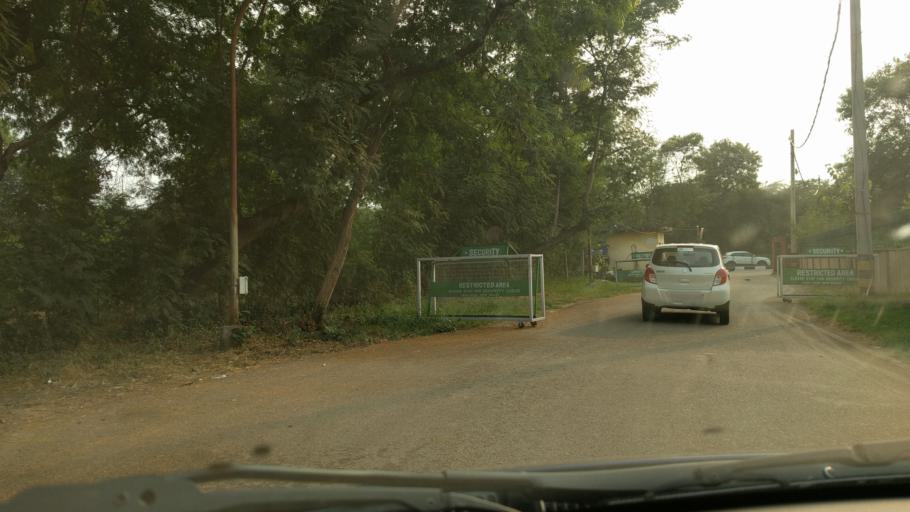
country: IN
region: NCT
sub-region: Central Delhi
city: Karol Bagh
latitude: 28.6277
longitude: 77.1530
